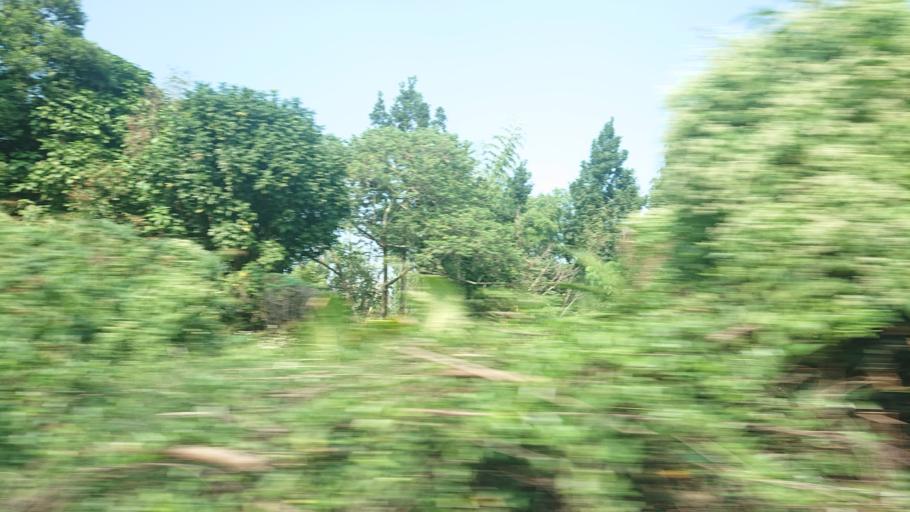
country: TW
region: Taiwan
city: Lugu
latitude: 23.7083
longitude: 120.6642
